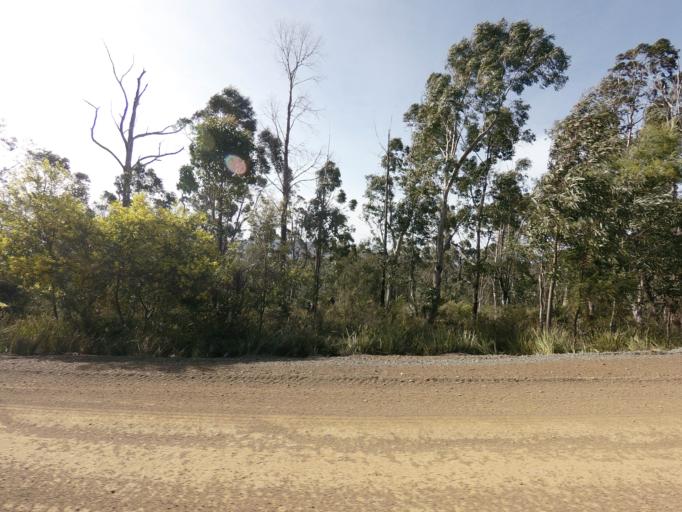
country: AU
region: Tasmania
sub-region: Kingborough
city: Kettering
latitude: -43.0823
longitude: 147.2647
